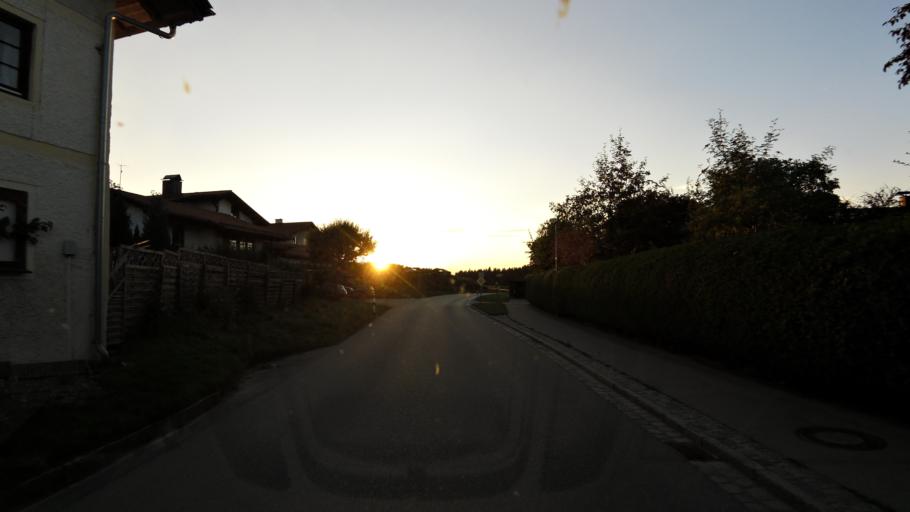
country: DE
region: Bavaria
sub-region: Upper Bavaria
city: Trostberg an der Alz
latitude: 48.0385
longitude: 12.5233
